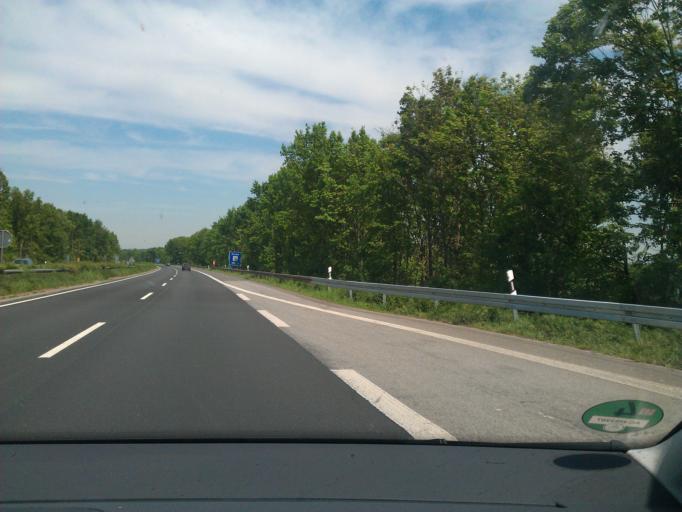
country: DE
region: North Rhine-Westphalia
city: Julich
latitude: 50.9183
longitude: 6.3294
